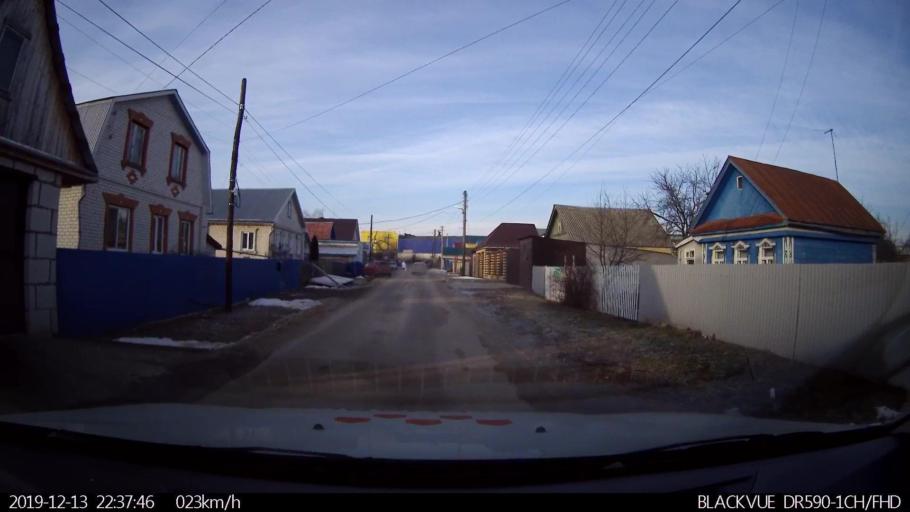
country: RU
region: Nizjnij Novgorod
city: Kstovo
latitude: 56.1747
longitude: 44.1674
